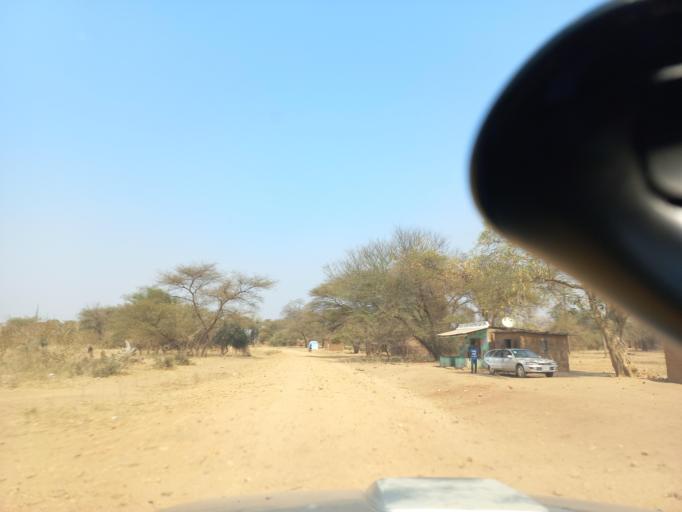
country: ZW
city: Chirundu
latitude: -15.9418
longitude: 28.8282
